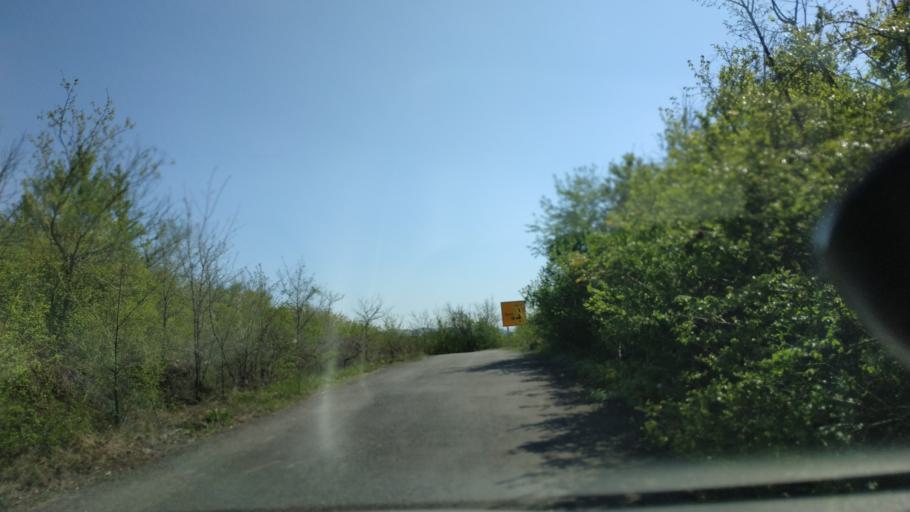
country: RS
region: Central Serbia
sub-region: Zajecarski Okrug
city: Soko Banja
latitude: 43.4928
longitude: 21.8732
